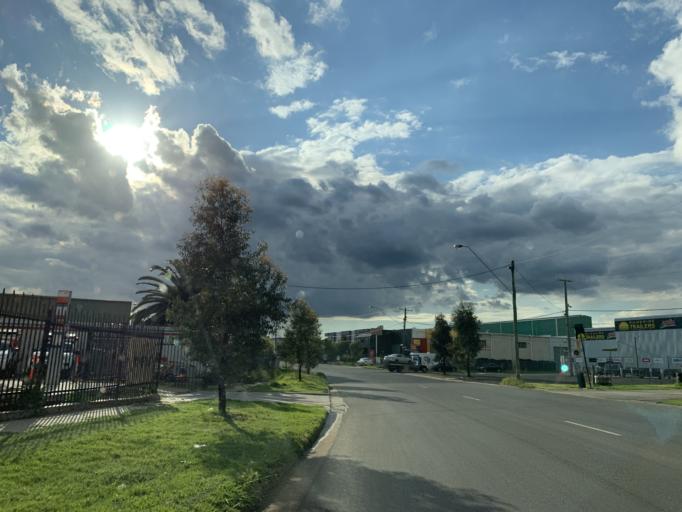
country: AU
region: Victoria
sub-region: Brimbank
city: Albion
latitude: -37.7664
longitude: 144.8462
